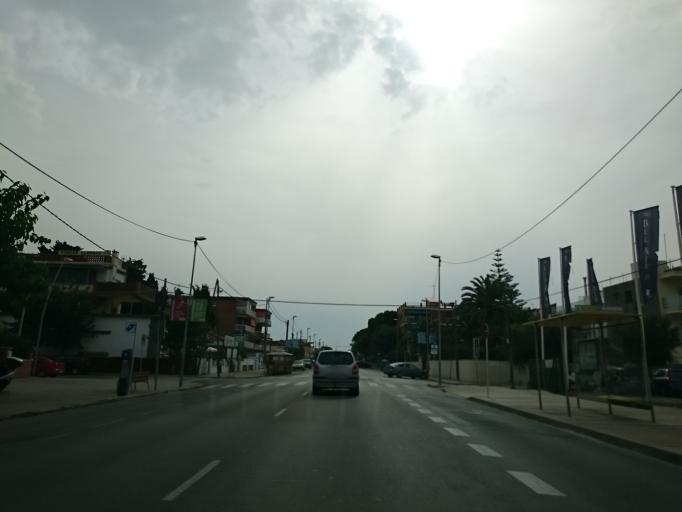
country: ES
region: Catalonia
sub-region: Provincia de Barcelona
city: Castelldefels
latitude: 41.2656
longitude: 1.9758
